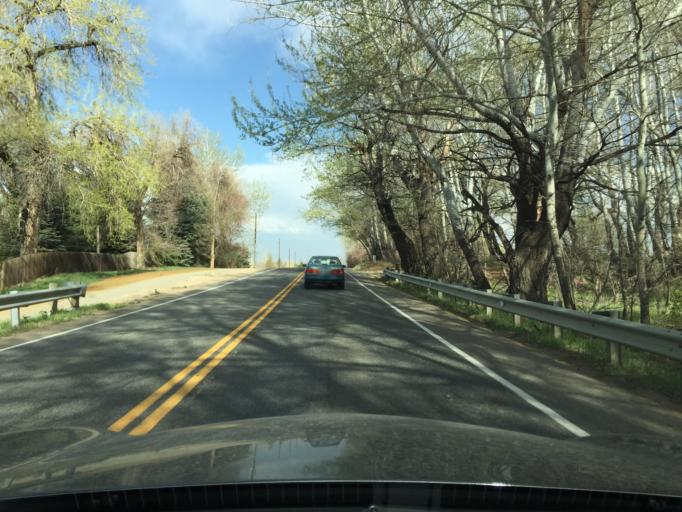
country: US
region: Colorado
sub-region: Boulder County
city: Niwot
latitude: 40.1017
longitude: -105.1377
